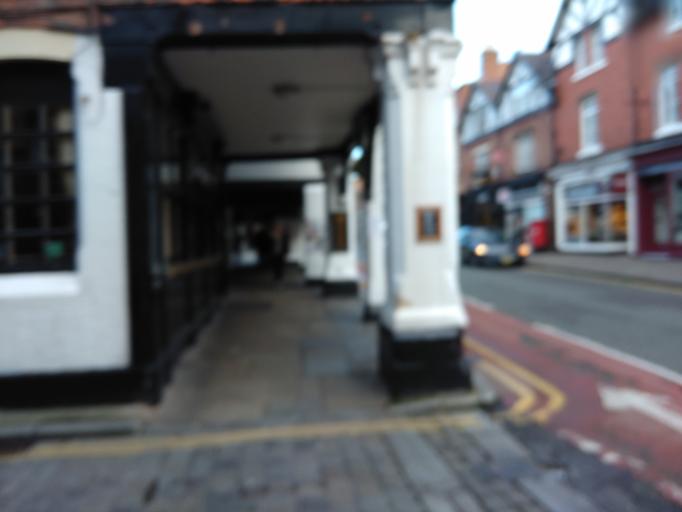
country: GB
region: England
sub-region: Cheshire West and Chester
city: Chester
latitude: 53.1931
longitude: -2.8929
